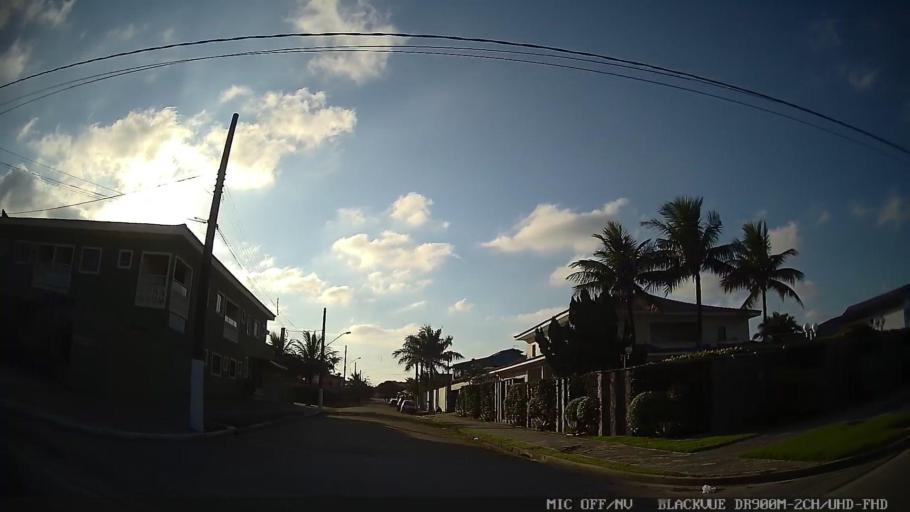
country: BR
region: Sao Paulo
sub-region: Peruibe
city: Peruibe
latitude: -24.2986
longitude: -46.9663
